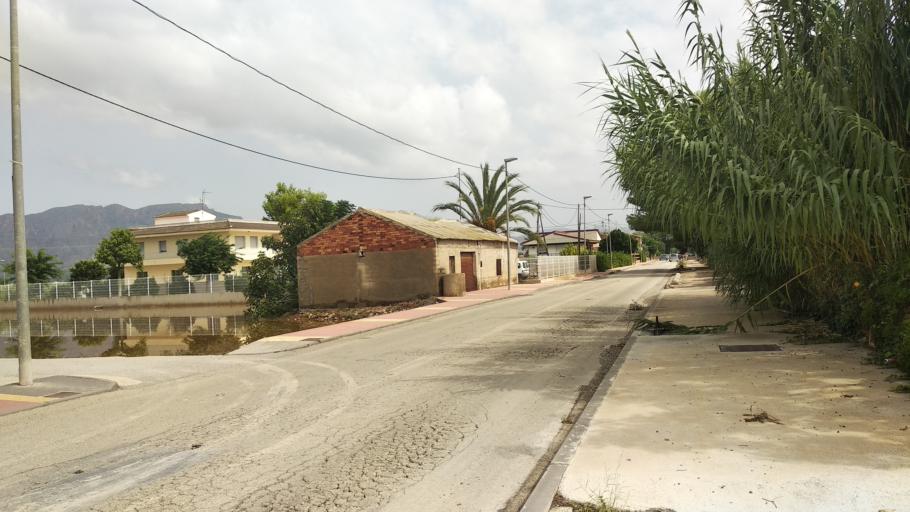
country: ES
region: Murcia
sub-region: Murcia
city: Santomera
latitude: 38.0444
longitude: -1.0391
